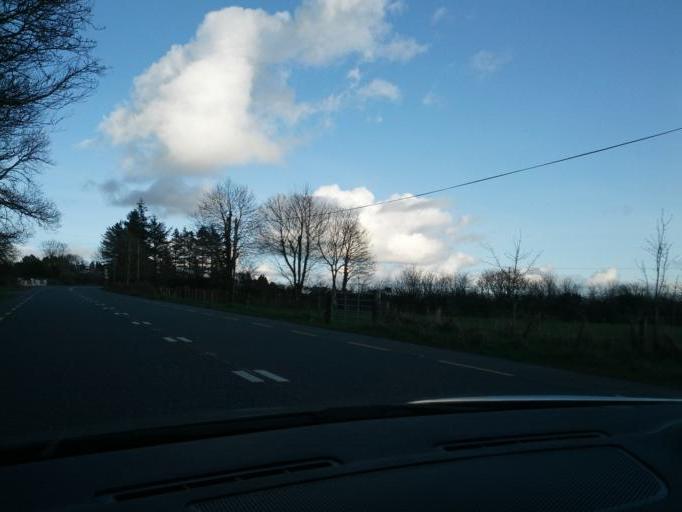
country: IE
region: Connaught
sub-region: Roscommon
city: Castlerea
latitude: 53.6870
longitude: -8.3738
